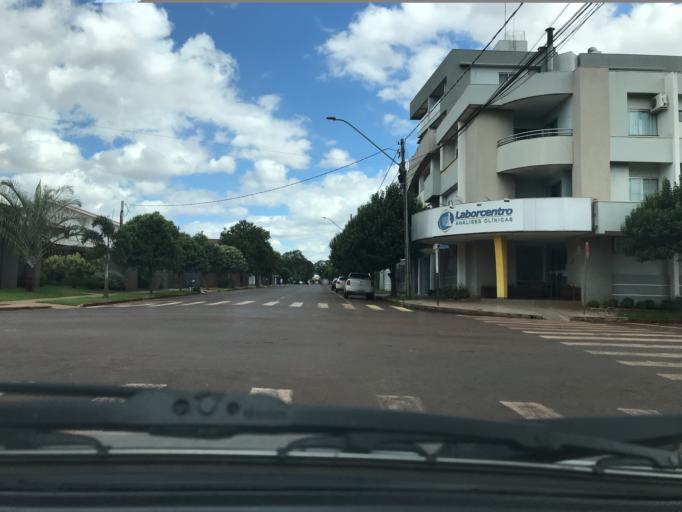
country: BR
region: Parana
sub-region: Palotina
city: Palotina
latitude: -24.2866
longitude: -53.8402
